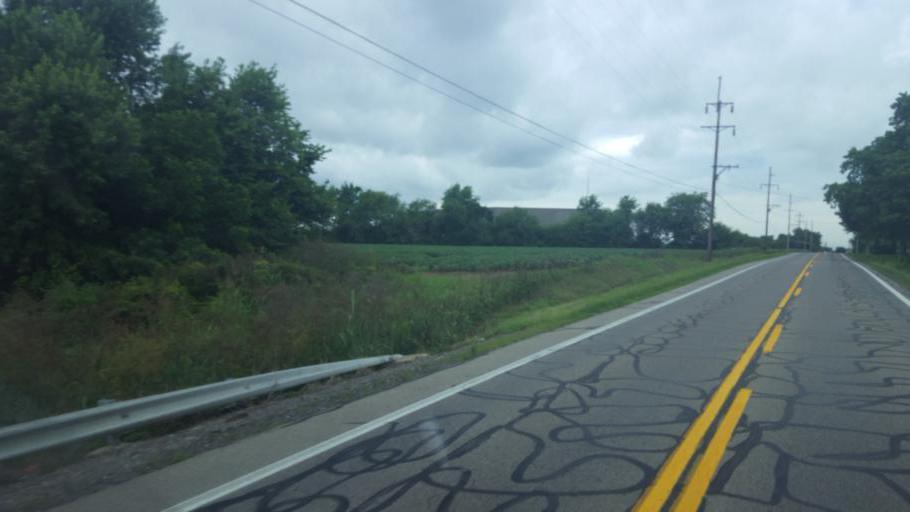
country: US
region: Ohio
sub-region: Pickaway County
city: Commercial Point
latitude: 39.7634
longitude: -83.0253
